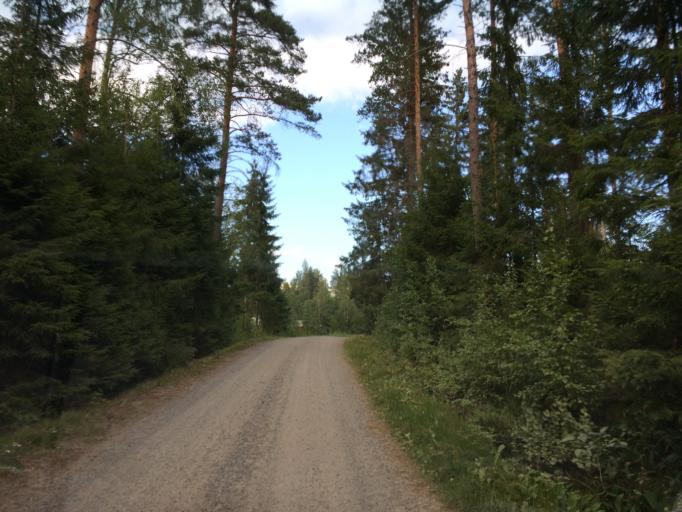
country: FI
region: Haeme
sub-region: Haemeenlinna
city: Hauho
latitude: 61.0791
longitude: 24.6498
